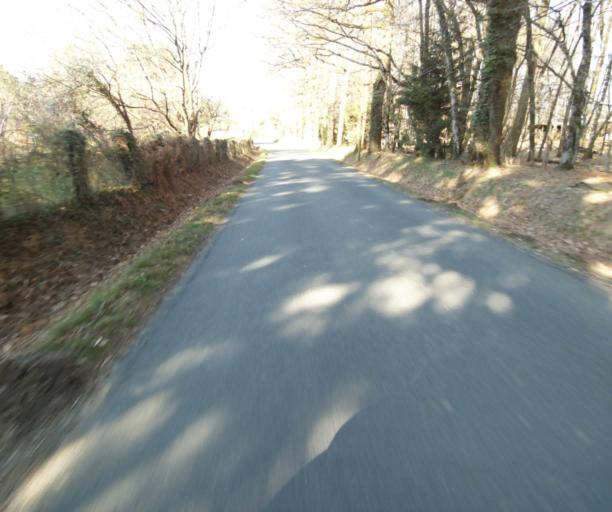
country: FR
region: Limousin
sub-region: Departement de la Correze
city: Saint-Clement
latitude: 45.3673
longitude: 1.6527
